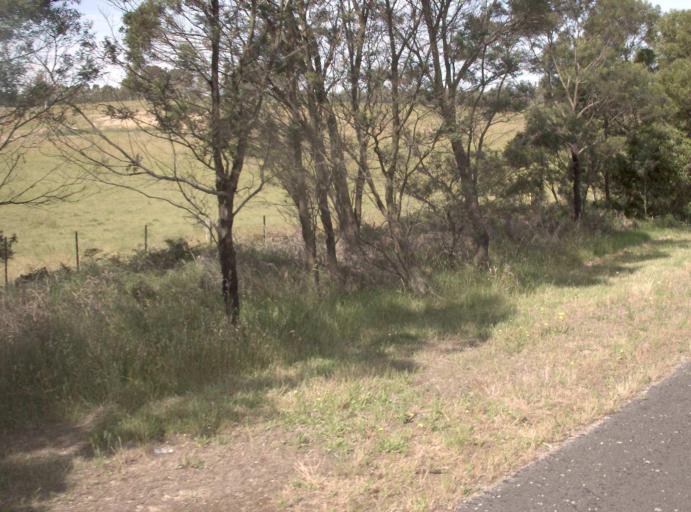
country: AU
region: Victoria
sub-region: East Gippsland
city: Lakes Entrance
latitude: -37.8189
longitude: 147.8216
